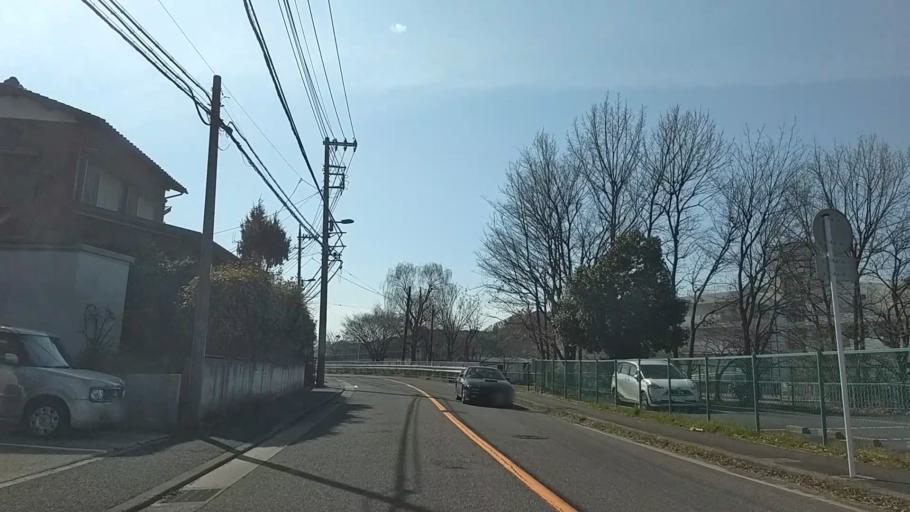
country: JP
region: Kanagawa
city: Yokohama
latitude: 35.4082
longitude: 139.5515
